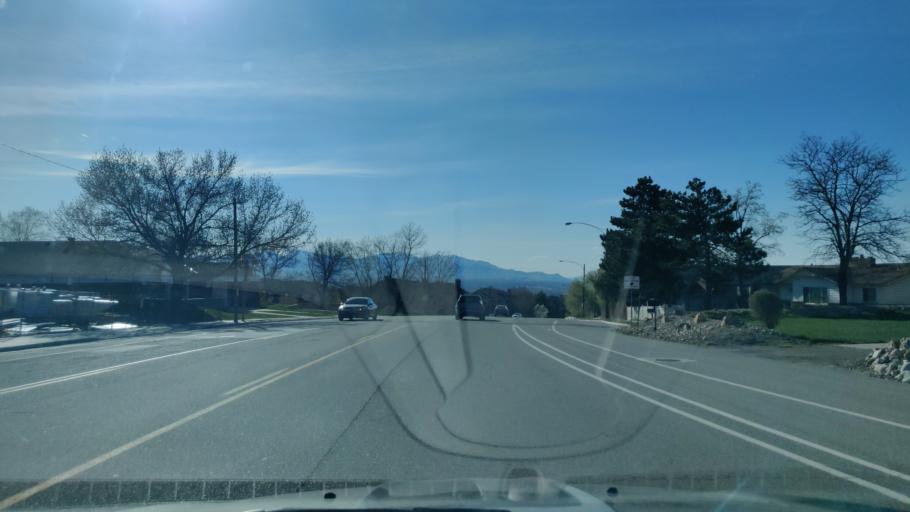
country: US
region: Utah
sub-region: Salt Lake County
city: Little Cottonwood Creek Valley
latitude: 40.6132
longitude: -111.8281
